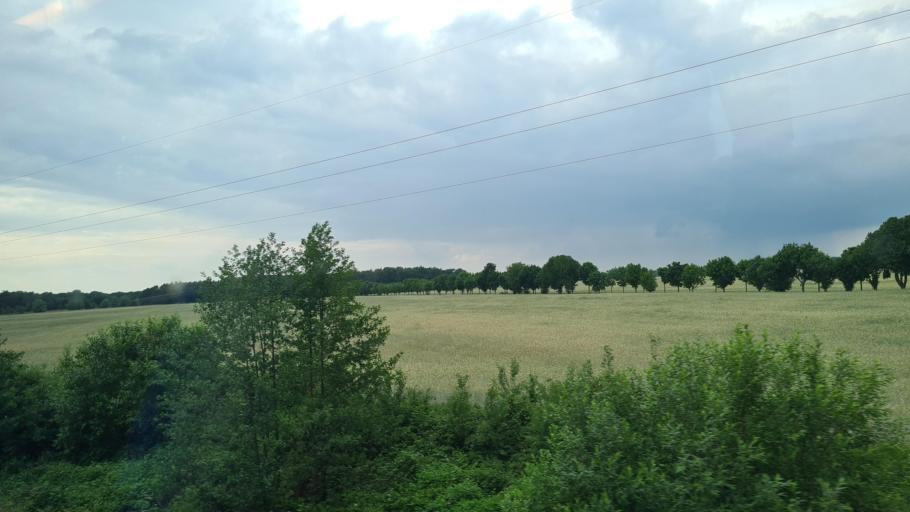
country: DE
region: Brandenburg
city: Schilda
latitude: 51.5877
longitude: 13.3247
